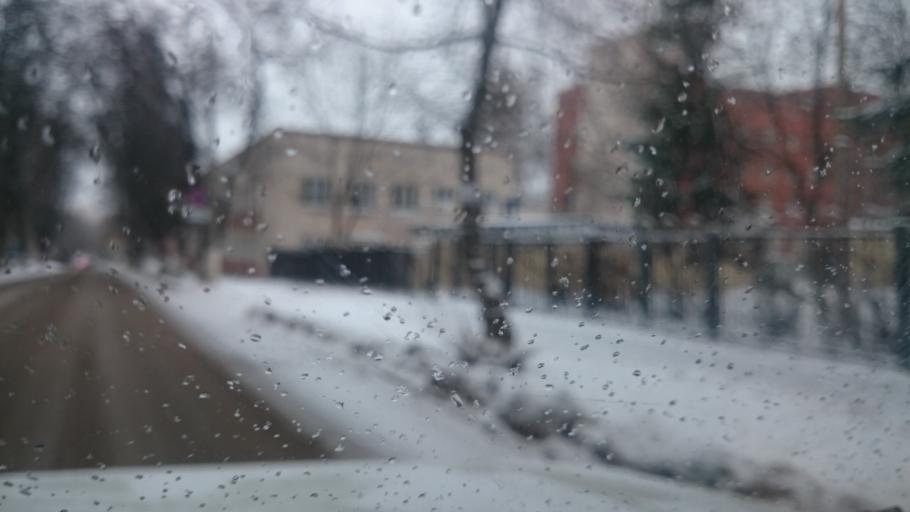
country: RU
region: Tula
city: Tula
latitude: 54.1858
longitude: 37.6016
